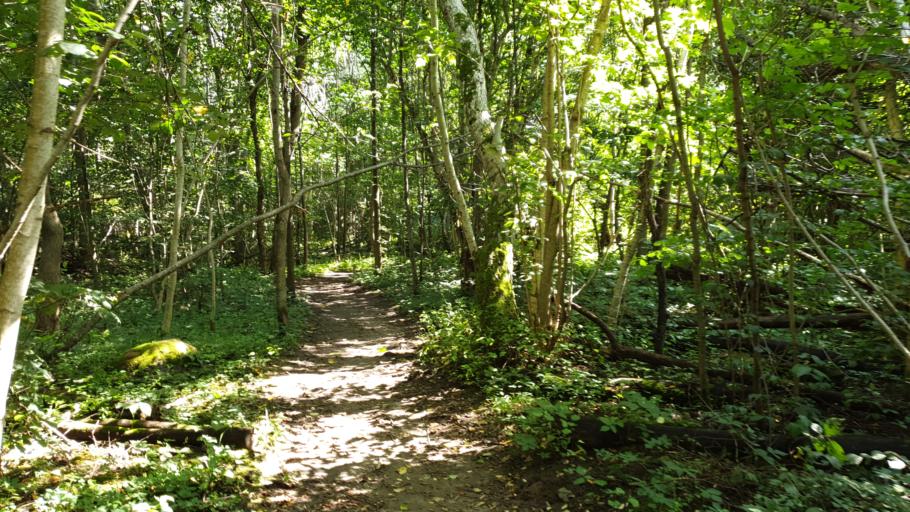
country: LT
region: Vilnius County
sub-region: Vilniaus Rajonas
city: Vievis
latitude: 54.8202
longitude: 24.9353
